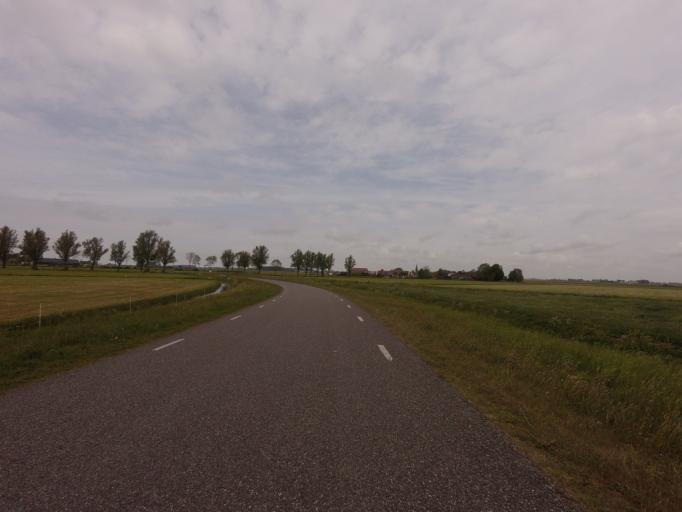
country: NL
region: Friesland
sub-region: Sudwest Fryslan
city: Bolsward
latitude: 53.0776
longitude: 5.4809
